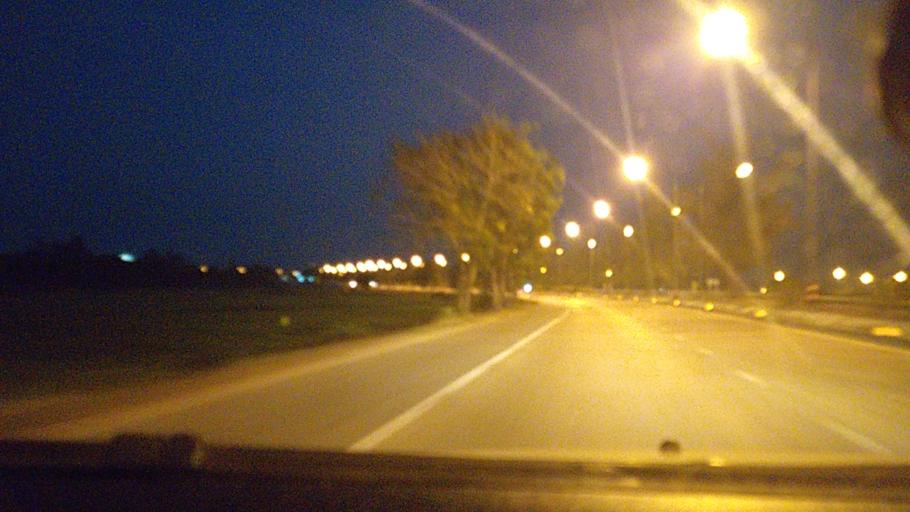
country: TH
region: Sing Buri
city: Sing Buri
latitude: 14.8721
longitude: 100.4272
